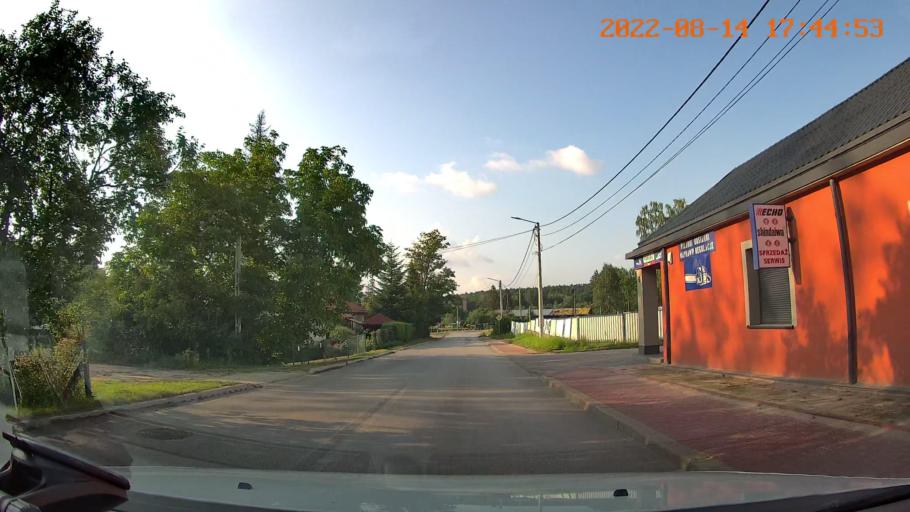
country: PL
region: Swietokrzyskie
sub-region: Powiat kielecki
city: Zagnansk
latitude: 50.9727
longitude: 20.6554
